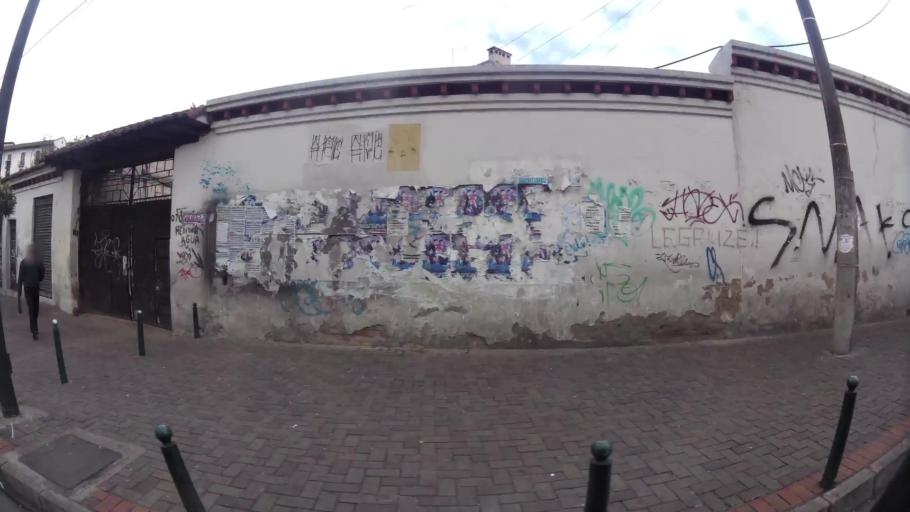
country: EC
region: Pichincha
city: Quito
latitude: -0.2233
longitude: -78.5080
